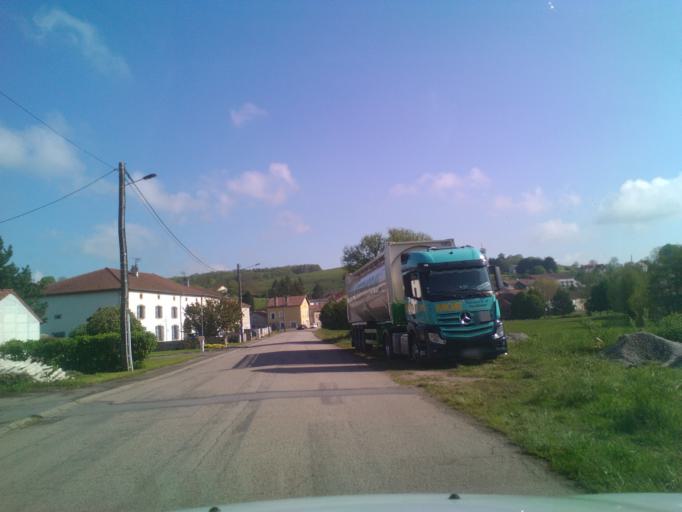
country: FR
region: Lorraine
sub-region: Departement des Vosges
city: Mirecourt
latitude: 48.3447
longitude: 6.1388
